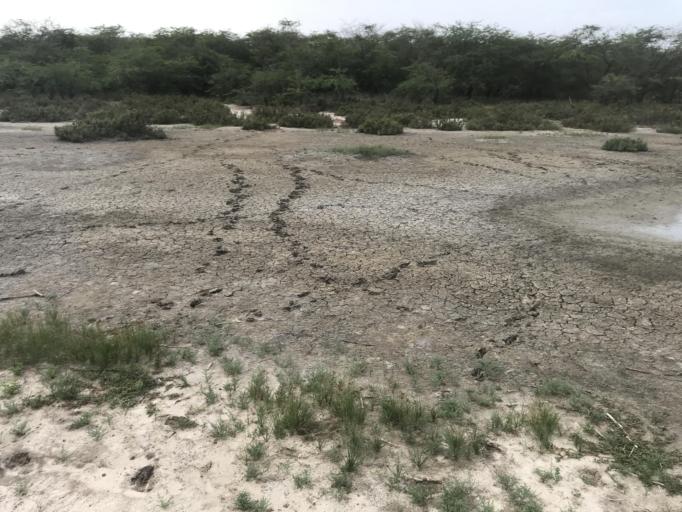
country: SN
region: Saint-Louis
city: Saint-Louis
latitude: 15.9273
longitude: -16.4669
